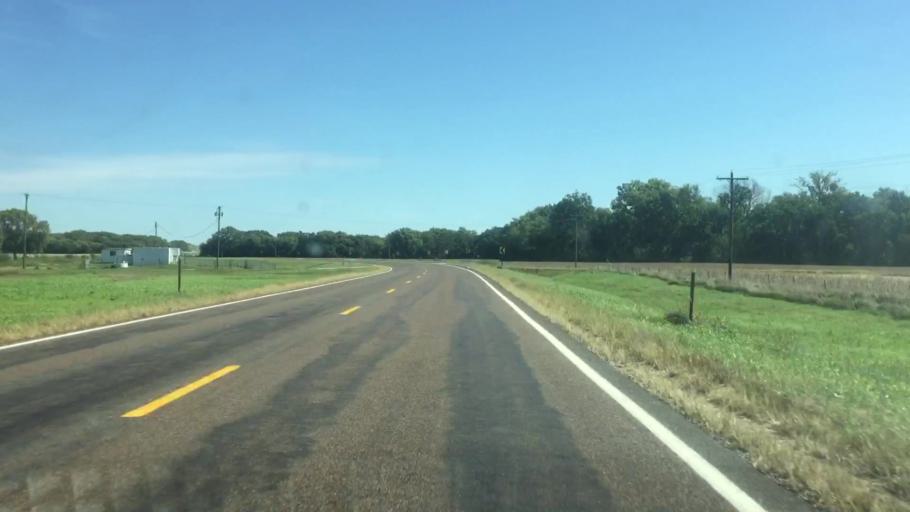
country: US
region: Nebraska
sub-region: Gage County
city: Wymore
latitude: 40.0446
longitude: -96.7947
